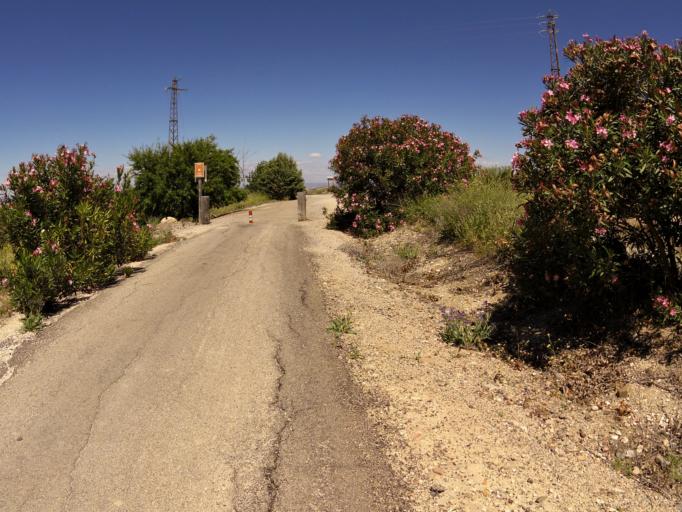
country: ES
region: Andalusia
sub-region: Provincia de Jaen
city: Torre del Campo
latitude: 37.7893
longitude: -3.8871
